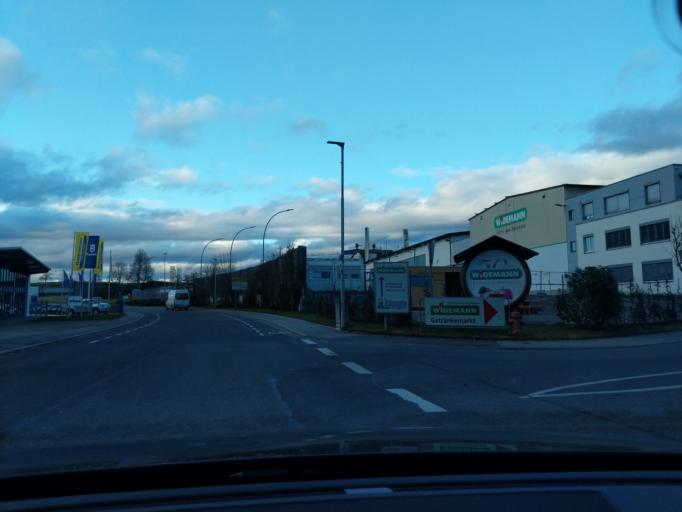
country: DE
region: Baden-Wuerttemberg
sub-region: Tuebingen Region
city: Bermatingen
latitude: 47.7271
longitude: 9.3210
